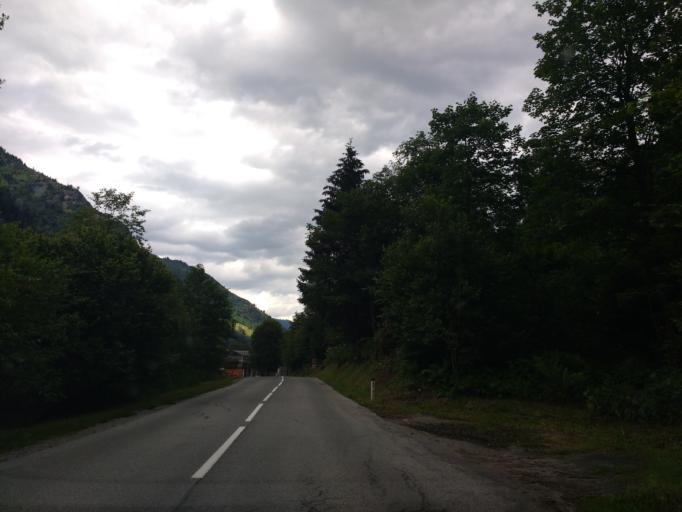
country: AT
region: Salzburg
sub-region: Politischer Bezirk Zell am See
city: Kaprun
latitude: 47.2274
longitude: 12.7265
